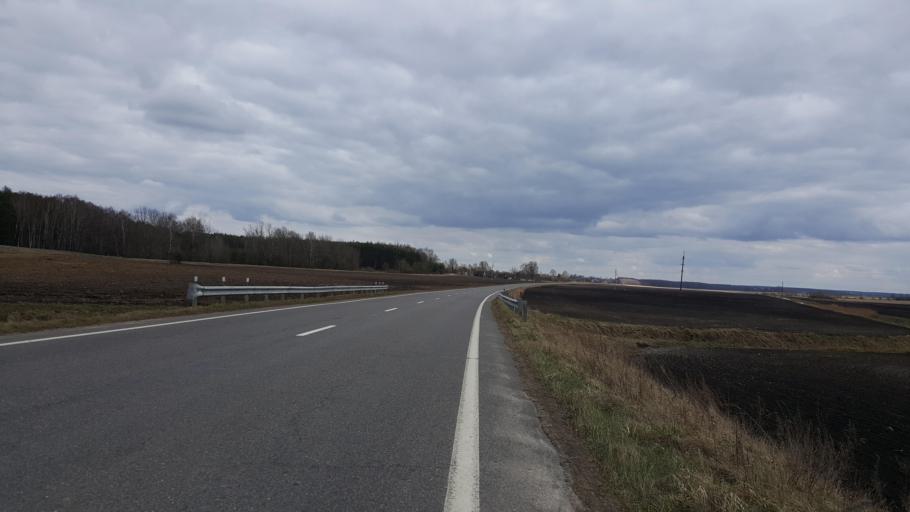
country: BY
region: Brest
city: Kamyanyets
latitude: 52.4669
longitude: 23.8270
